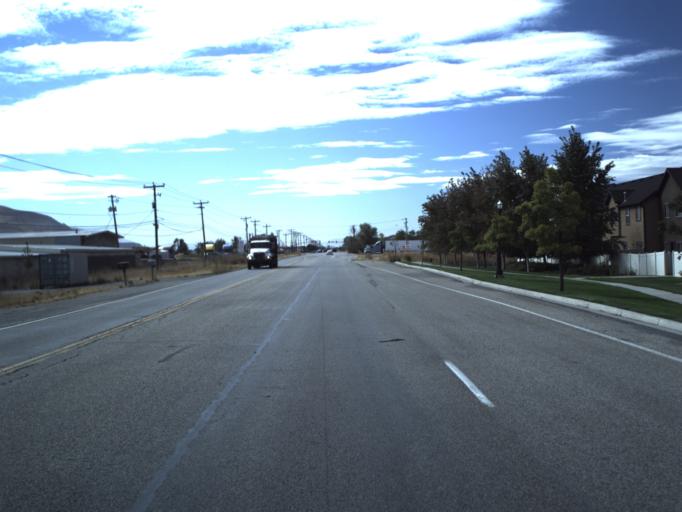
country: US
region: Utah
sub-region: Davis County
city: North Salt Lake
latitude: 40.8665
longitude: -111.9300
